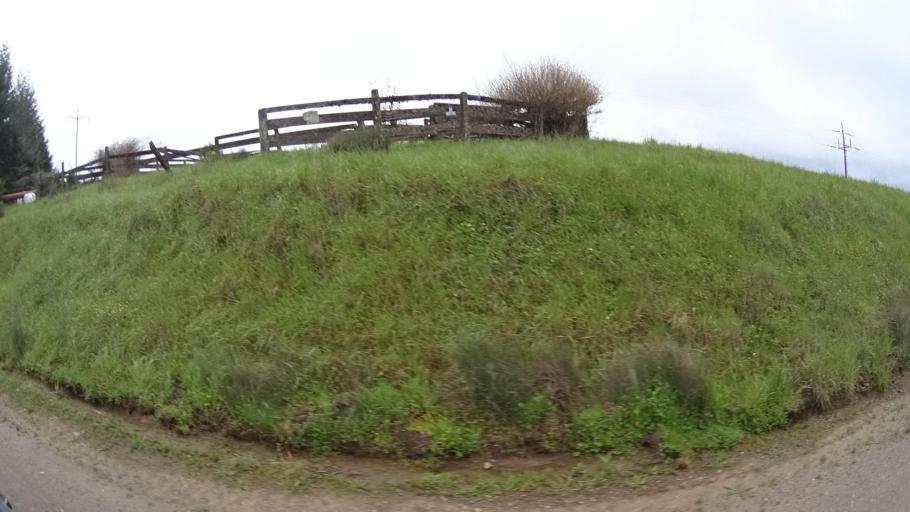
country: US
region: California
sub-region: Humboldt County
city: Redway
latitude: 40.2167
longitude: -123.7522
